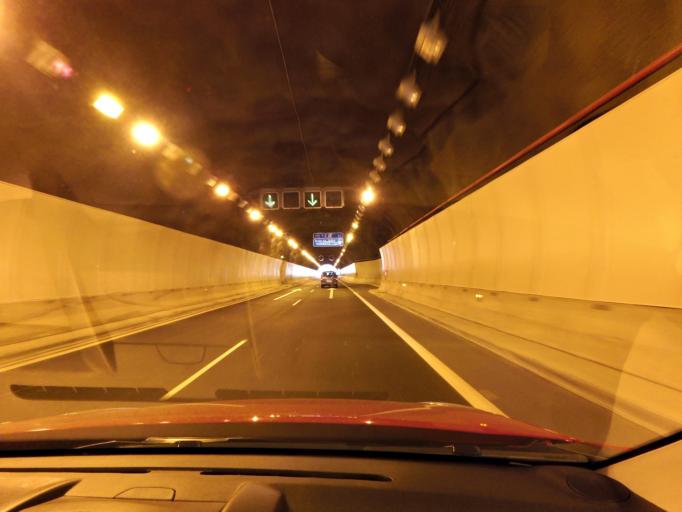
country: ES
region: Canary Islands
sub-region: Provincia de Las Palmas
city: Puerto Rico
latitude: 27.7990
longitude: -15.7033
